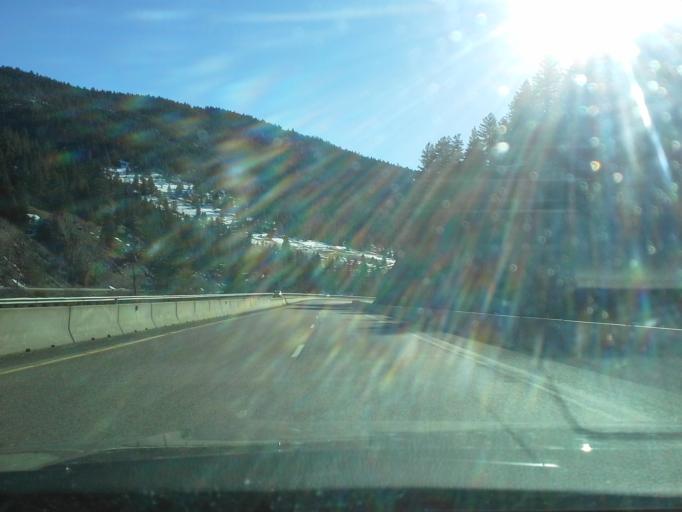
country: US
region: Montana
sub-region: Lewis and Clark County
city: Helena Valley Northwest
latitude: 46.9636
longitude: -112.0950
